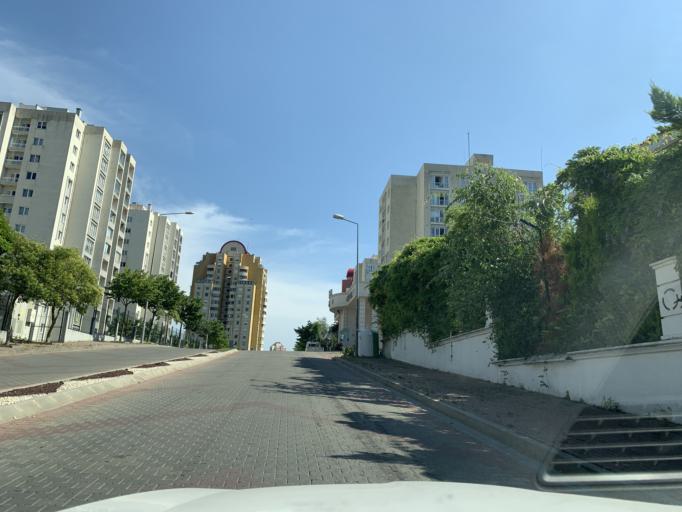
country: TR
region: Istanbul
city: Esenyurt
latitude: 41.0739
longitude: 28.6790
